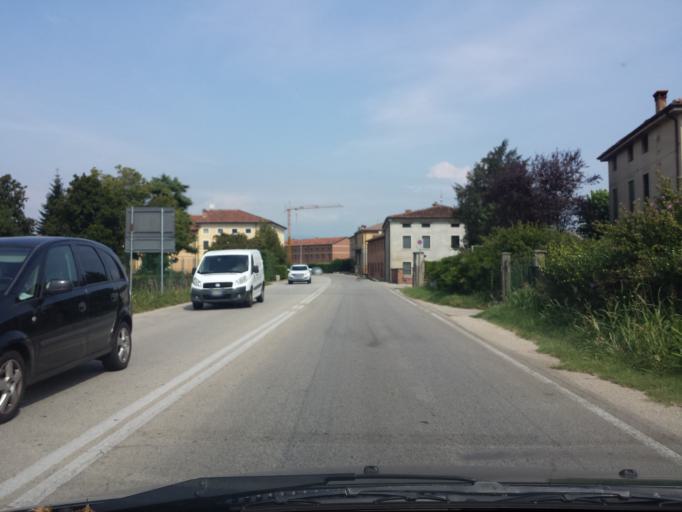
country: IT
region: Veneto
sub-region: Provincia di Vicenza
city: Monticello Conte Otto
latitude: 45.5978
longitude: 11.5571
